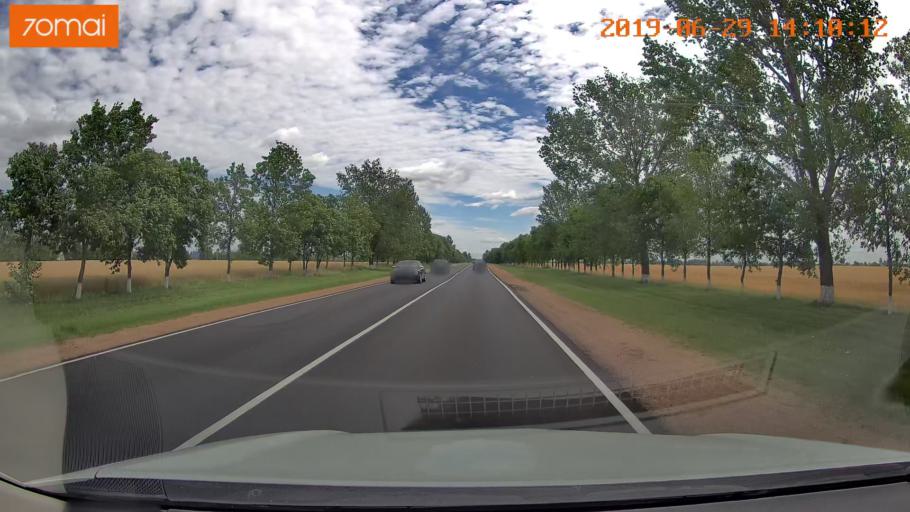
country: BY
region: Minsk
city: Salihorsk
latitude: 52.8323
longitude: 27.4921
